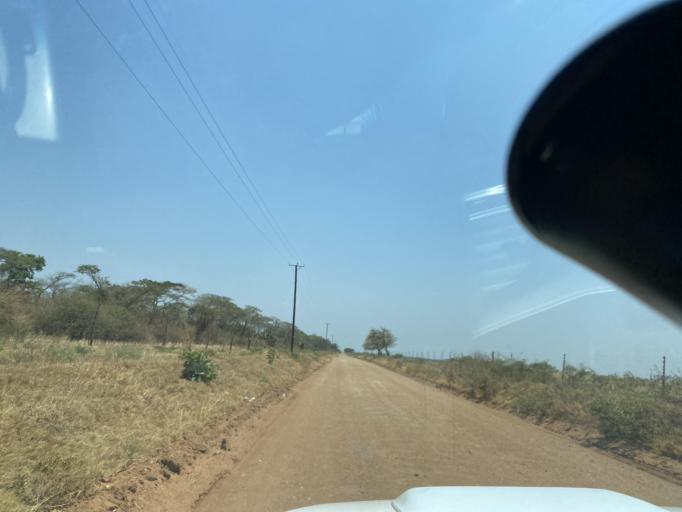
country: ZM
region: Lusaka
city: Lusaka
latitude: -15.4382
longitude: 28.0651
